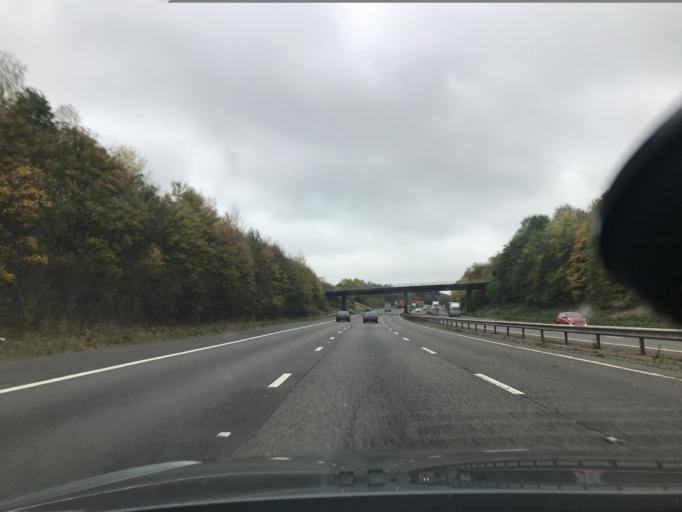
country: GB
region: England
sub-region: Warwickshire
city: Wroxall
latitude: 52.2909
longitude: -1.6738
